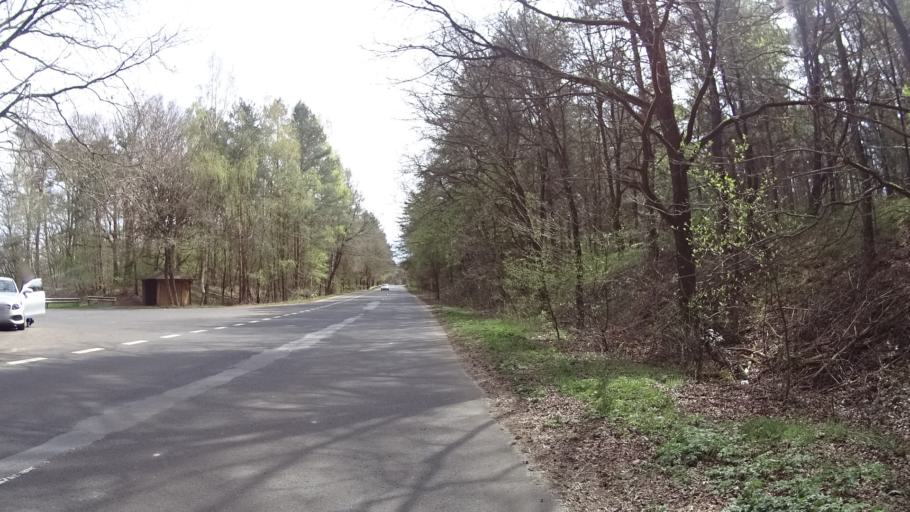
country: DE
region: Lower Saxony
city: Emsburen
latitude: 52.4167
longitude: 7.3611
